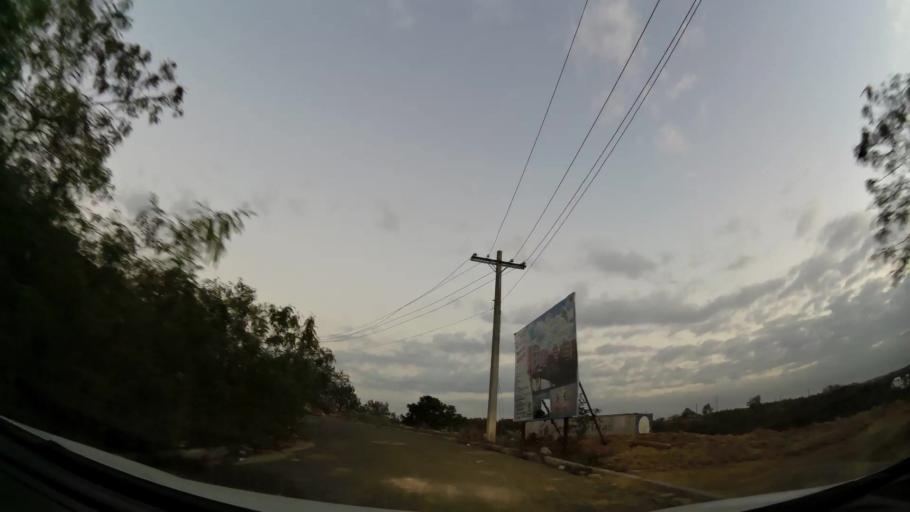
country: DO
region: Nacional
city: La Agustina
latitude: 18.5425
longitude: -69.9470
